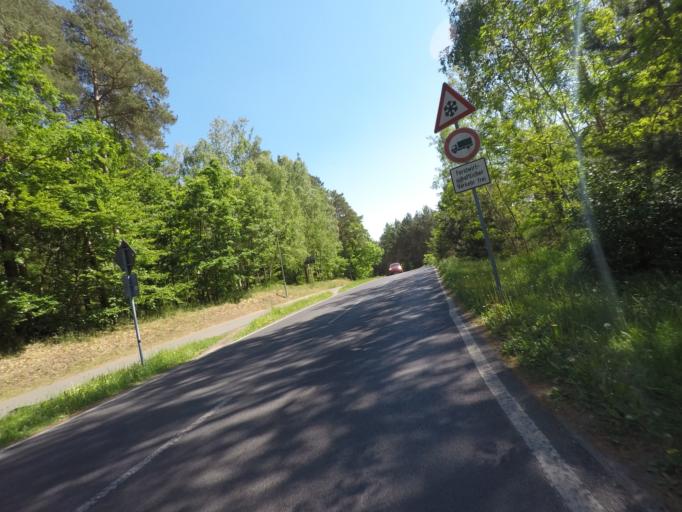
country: DE
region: Brandenburg
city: Eberswalde
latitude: 52.8281
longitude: 13.7686
